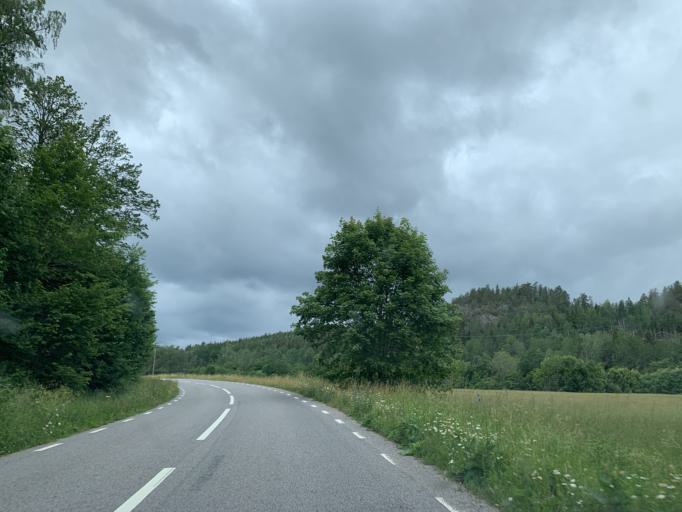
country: SE
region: Kalmar
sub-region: Vasterviks Kommun
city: Overum
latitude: 58.0164
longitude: 16.1645
